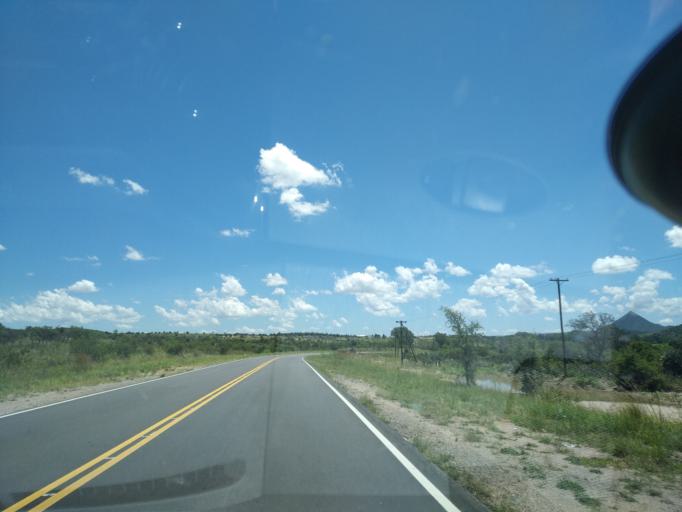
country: AR
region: Cordoba
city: Salsacate
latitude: -31.3498
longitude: -65.0860
